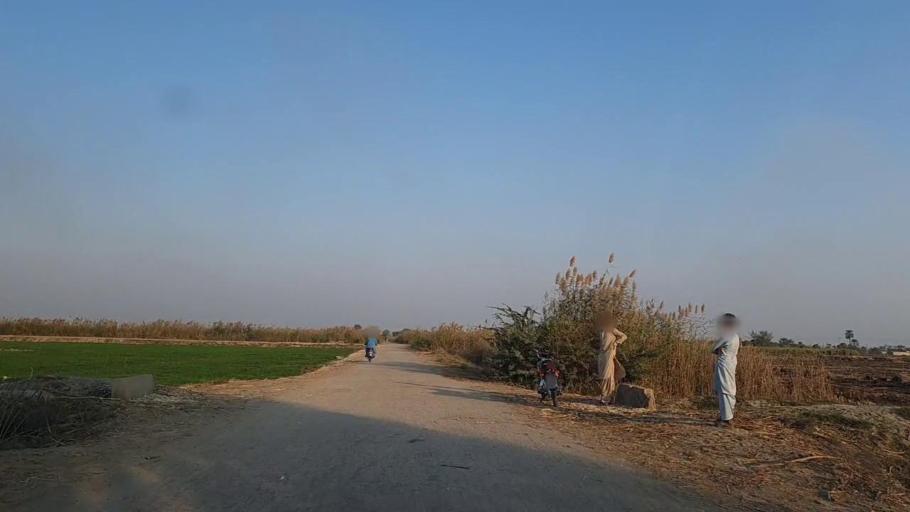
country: PK
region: Sindh
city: Daur
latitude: 26.5106
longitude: 68.3002
